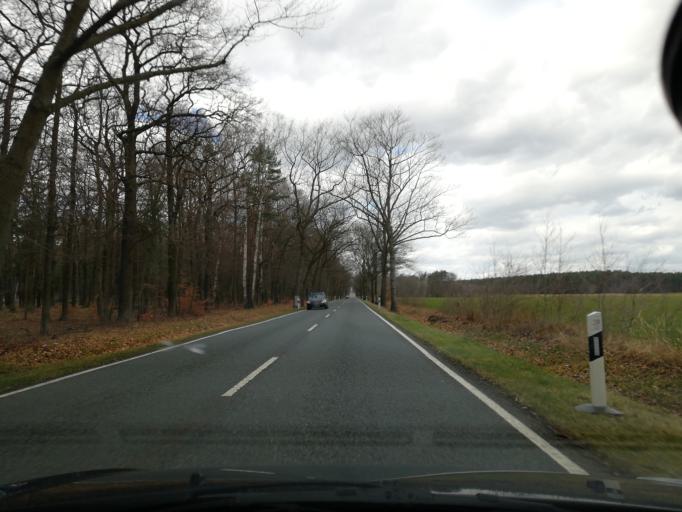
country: DE
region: Brandenburg
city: Altdobern
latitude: 51.7015
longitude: 14.0724
